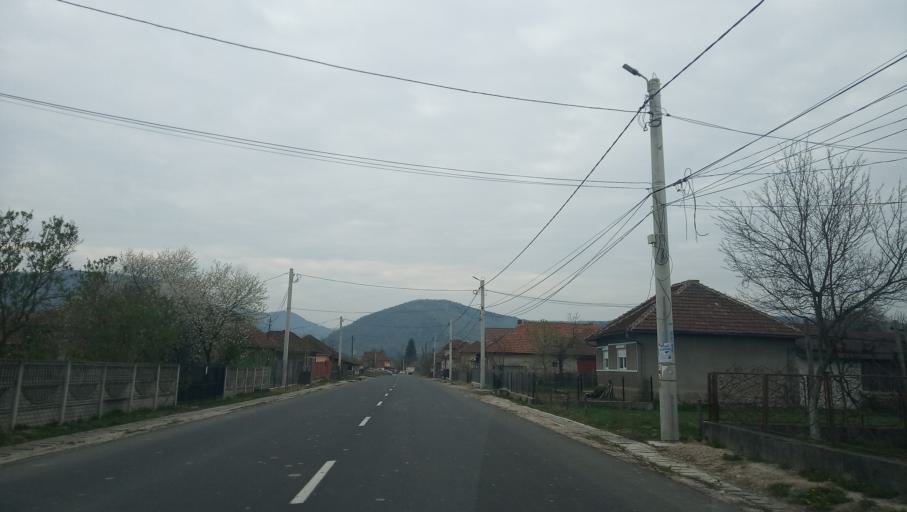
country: RO
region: Arad
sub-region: Comuna Varfurile
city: Varfurile
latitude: 46.3095
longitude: 22.5301
